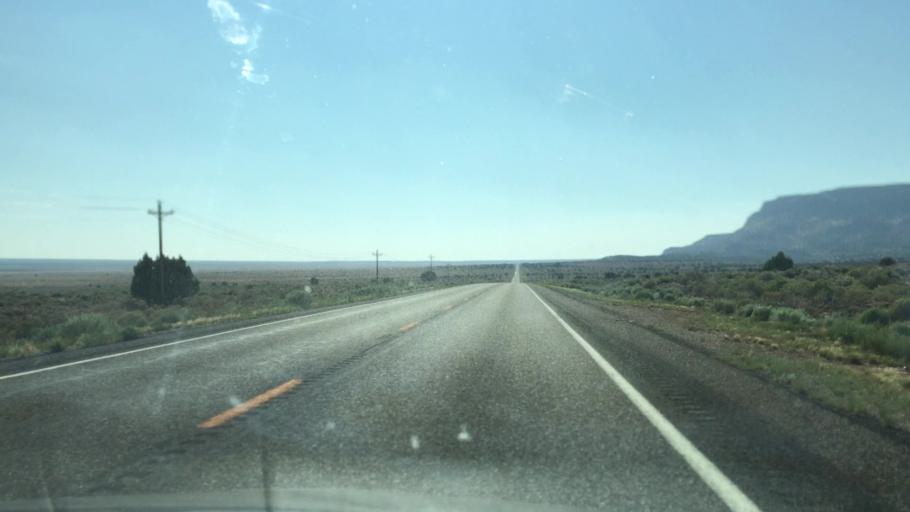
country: US
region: Arizona
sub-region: Coconino County
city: Fredonia
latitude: 36.8577
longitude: -112.7397
